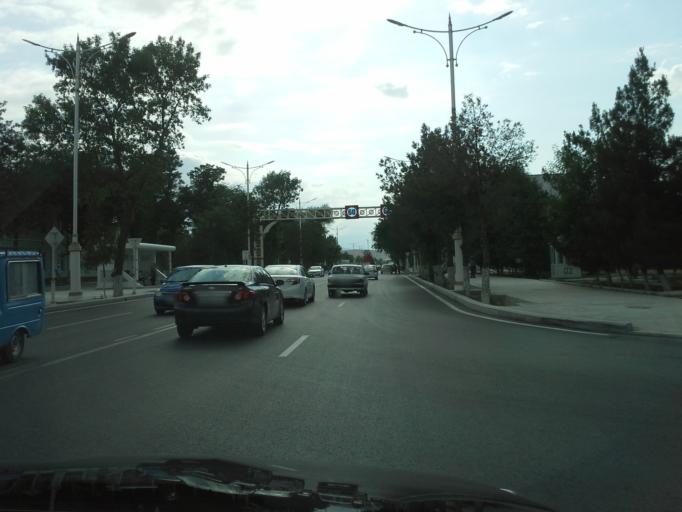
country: TM
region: Ahal
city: Ashgabat
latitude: 37.9581
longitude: 58.3486
